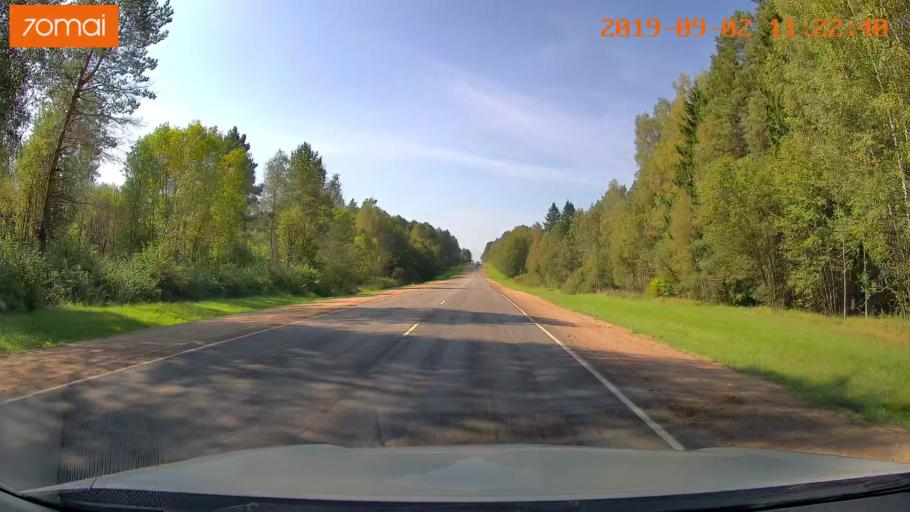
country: RU
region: Smolensk
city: Roslavl'
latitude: 54.0238
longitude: 33.0082
